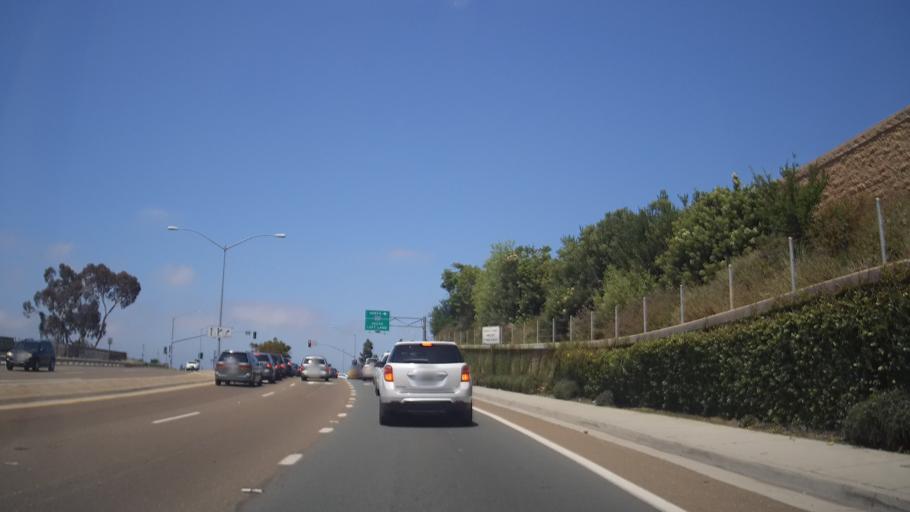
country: US
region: California
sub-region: San Diego County
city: Bonita
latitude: 32.6066
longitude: -117.0337
